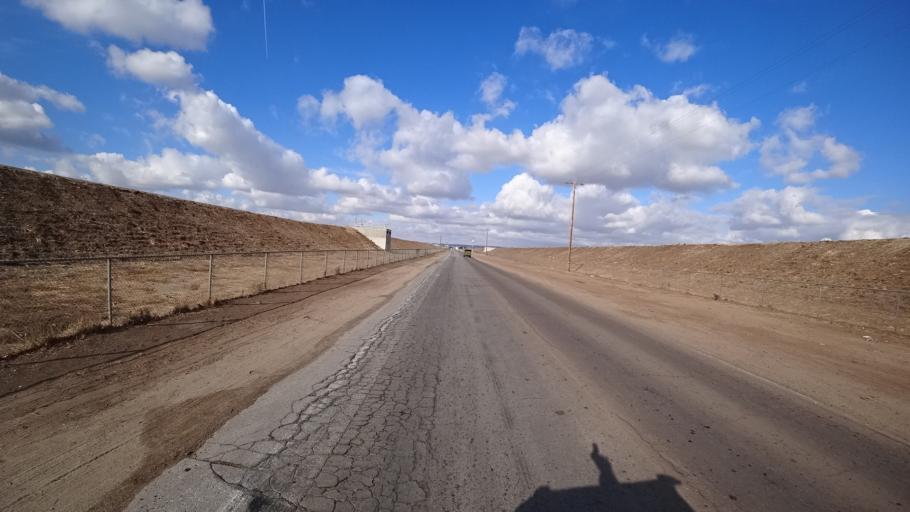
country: US
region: California
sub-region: Kern County
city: Bakersfield
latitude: 35.3280
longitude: -118.9677
